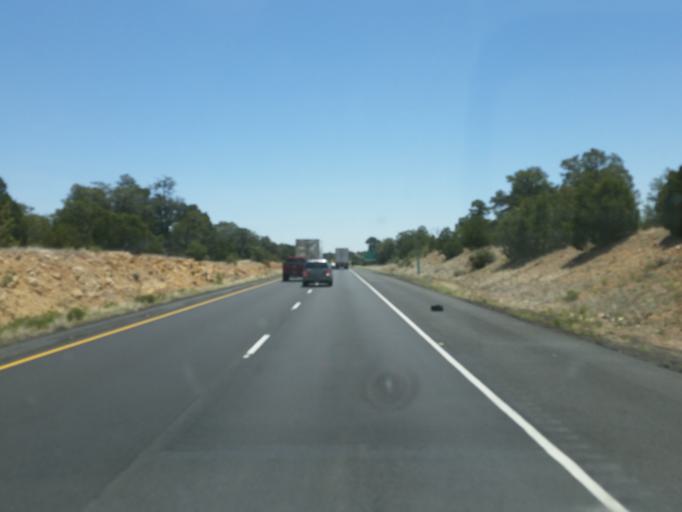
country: US
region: Arizona
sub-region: Coconino County
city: Flagstaff
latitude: 35.2055
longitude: -111.4986
